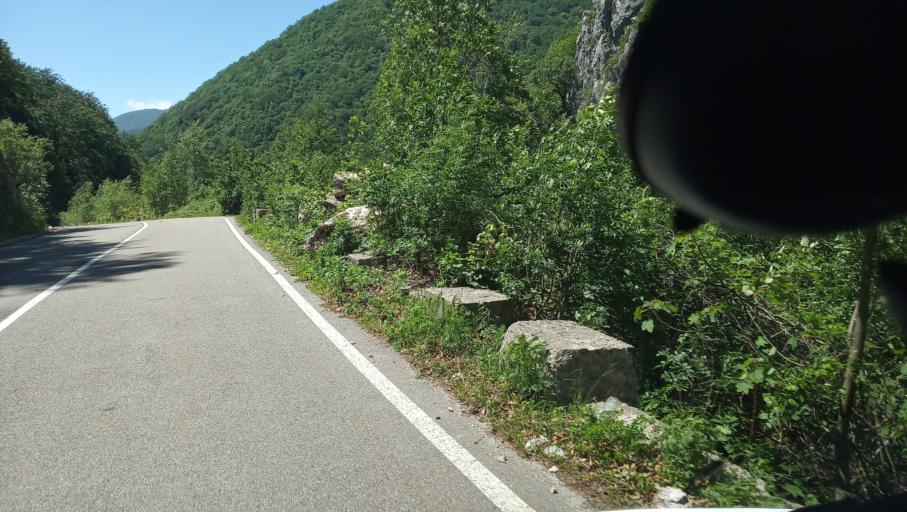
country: RO
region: Mehedinti
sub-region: Comuna Isverna
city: Isverna
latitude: 45.0547
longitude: 22.6008
